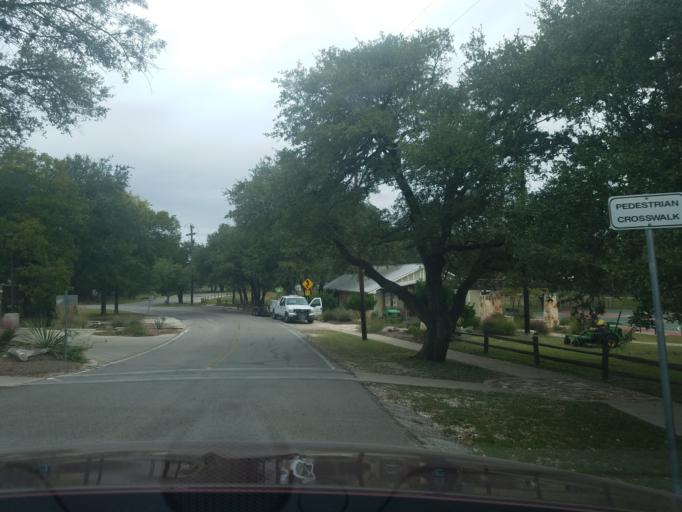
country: US
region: Texas
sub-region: Williamson County
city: Anderson Mill
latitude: 30.4788
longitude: -97.8130
